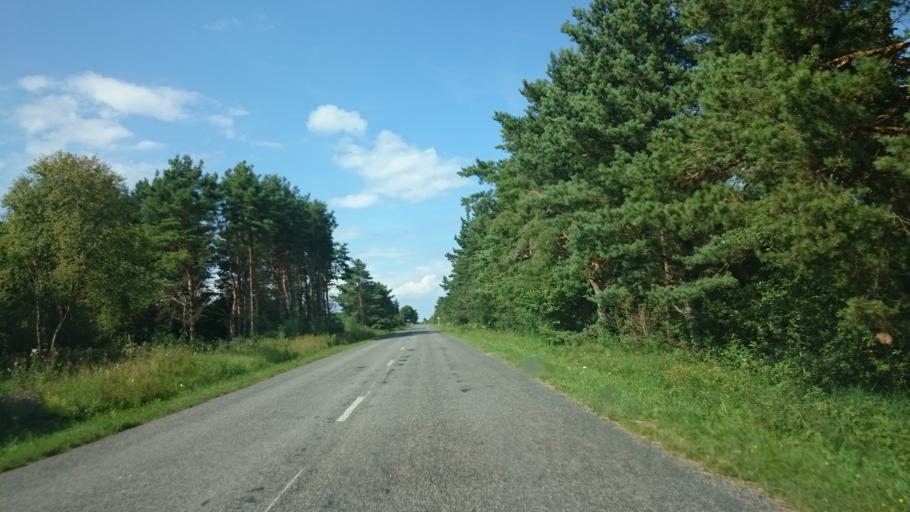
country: EE
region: Saare
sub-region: Orissaare vald
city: Orissaare
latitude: 58.5779
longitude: 23.0282
